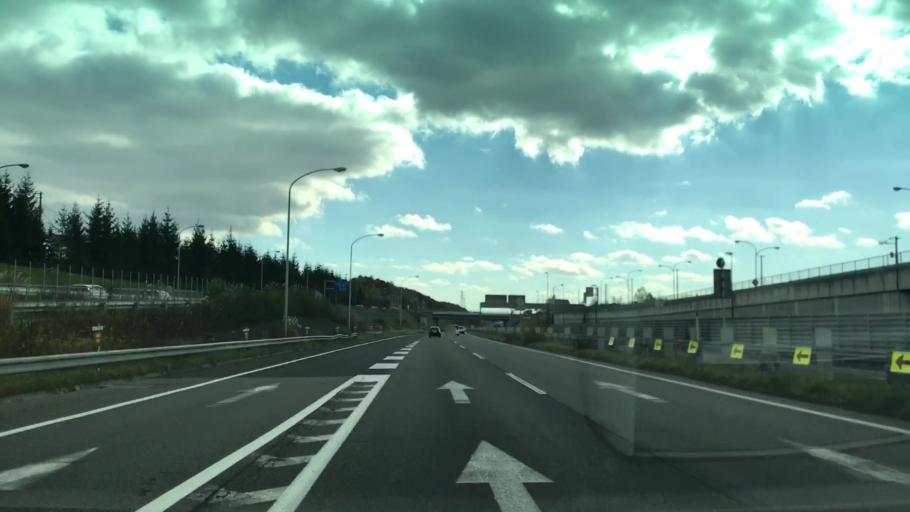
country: JP
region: Hokkaido
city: Kitahiroshima
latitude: 43.0128
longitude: 141.4652
